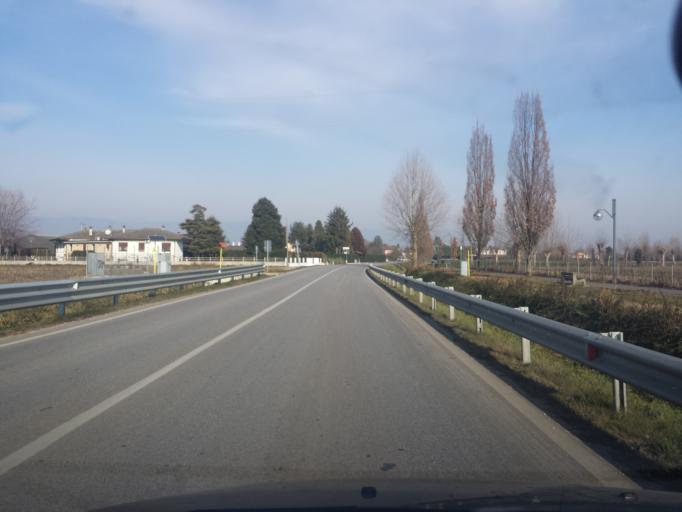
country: IT
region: Veneto
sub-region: Provincia di Vicenza
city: Poianella
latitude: 45.6369
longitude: 11.6266
